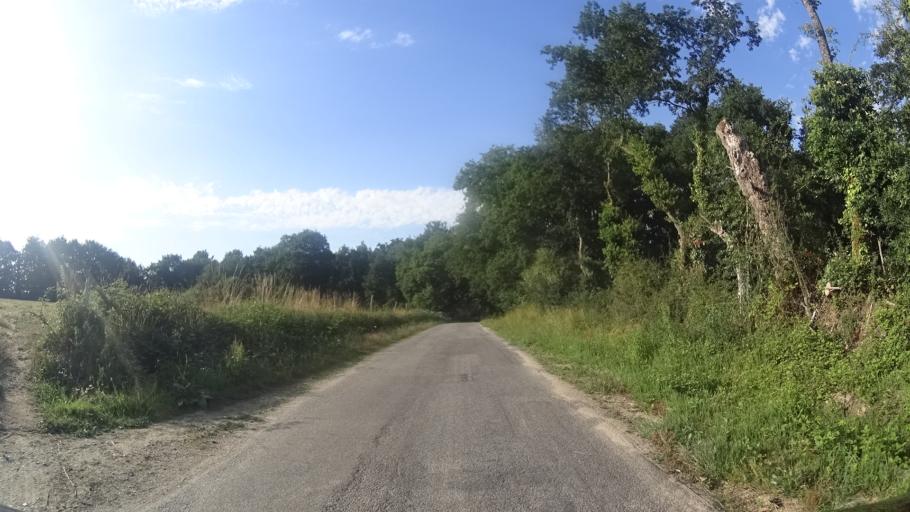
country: FR
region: Brittany
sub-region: Departement du Morbihan
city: Saint-Jean-la-Poterie
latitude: 47.6393
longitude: -2.1436
